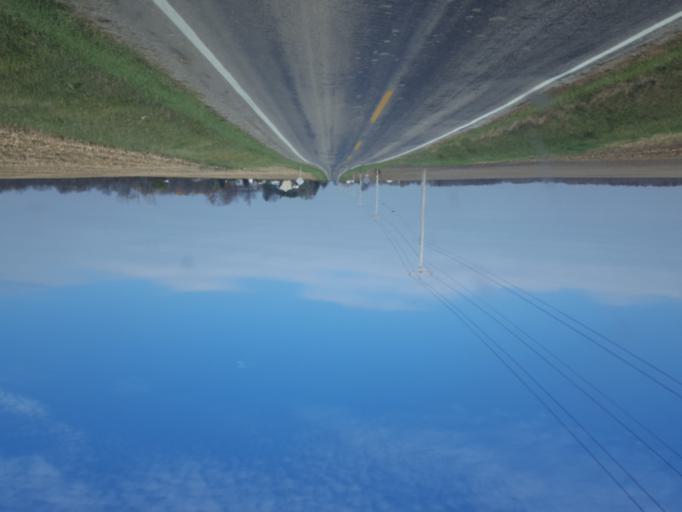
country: US
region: Ohio
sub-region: Lorain County
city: Camden
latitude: 41.2383
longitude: -82.2562
